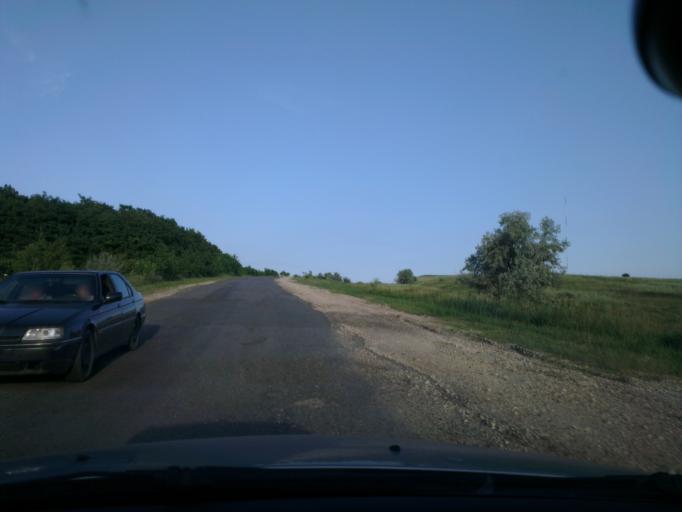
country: MD
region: Cantemir
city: Visniovca
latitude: 46.3656
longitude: 28.3903
